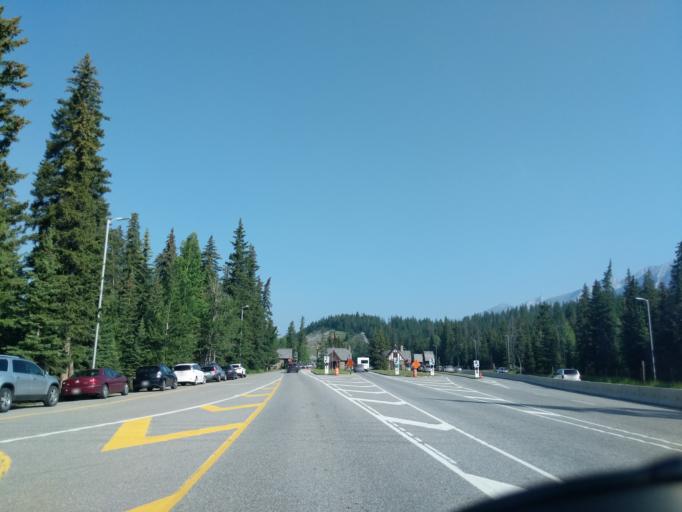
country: CA
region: Alberta
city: Canmore
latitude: 51.1336
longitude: -115.4057
